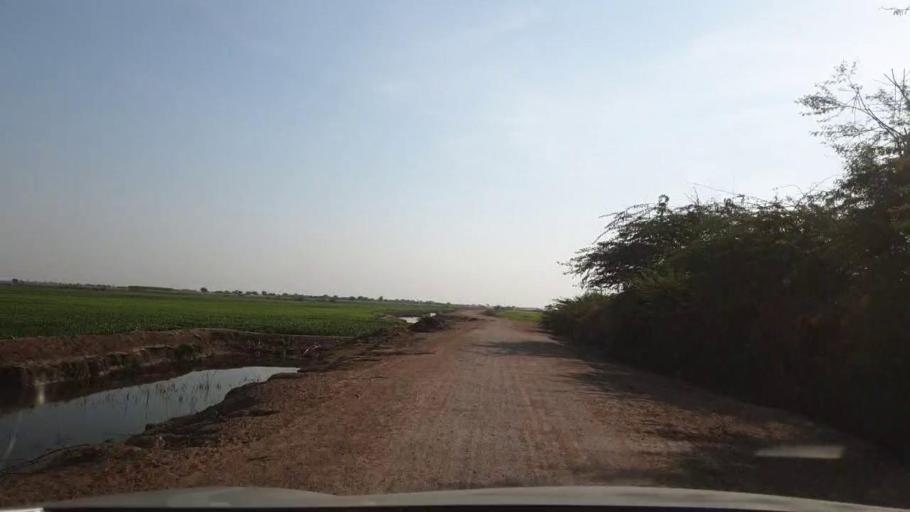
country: PK
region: Sindh
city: Berani
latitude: 25.7115
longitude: 68.8065
